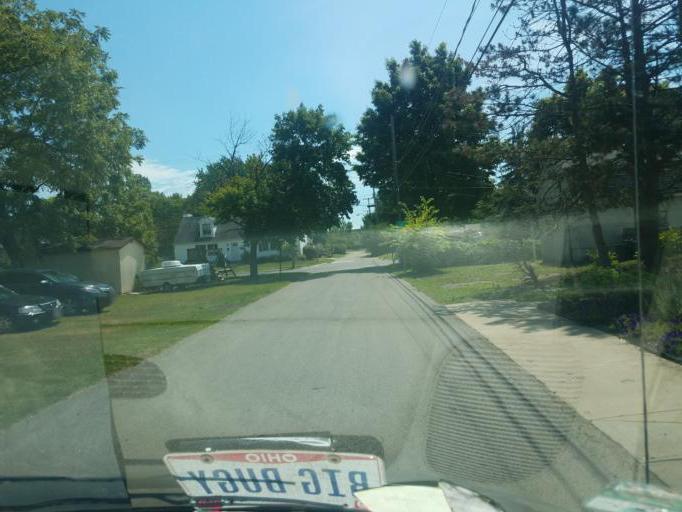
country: US
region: Ohio
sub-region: Franklin County
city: Grove City
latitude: 39.8803
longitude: -83.0916
